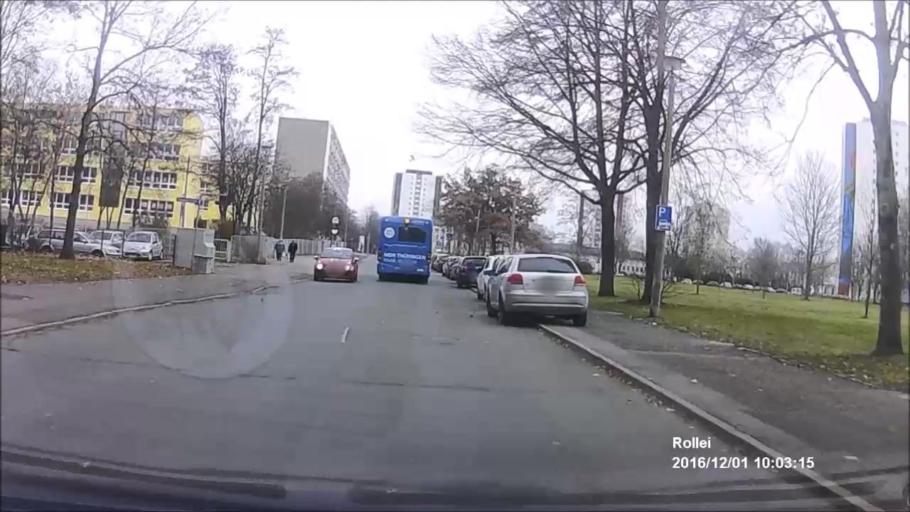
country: DE
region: Thuringia
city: Erfurt
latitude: 51.0120
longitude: 10.9976
